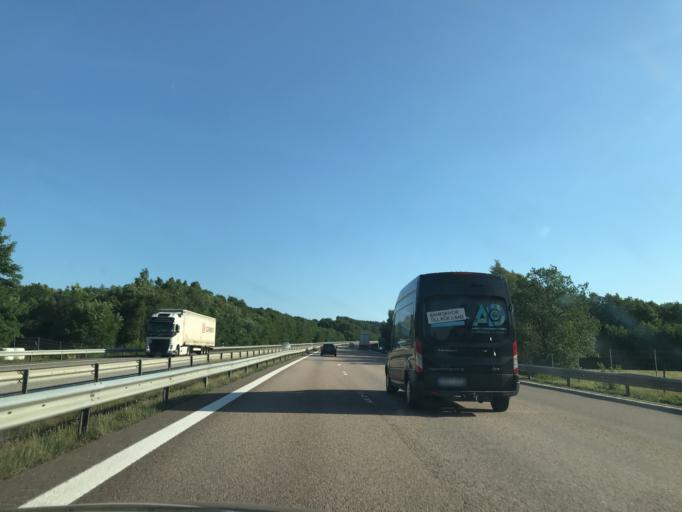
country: SE
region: Skane
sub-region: Bastads Kommun
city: Forslov
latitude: 56.3364
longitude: 12.9148
